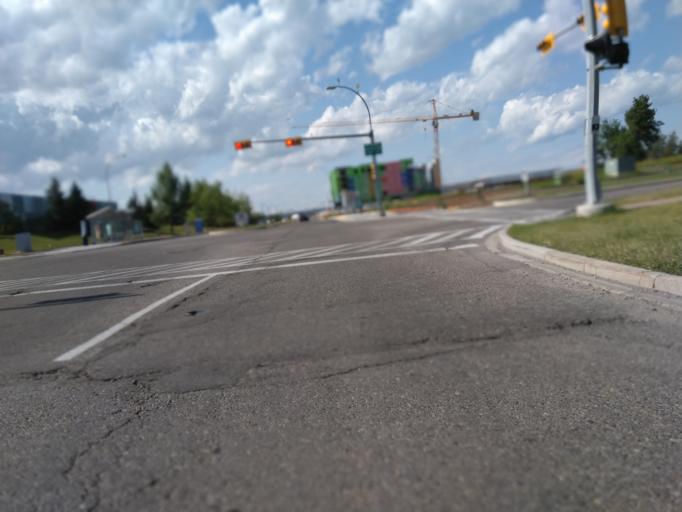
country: CA
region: Alberta
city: Calgary
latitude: 51.0750
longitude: -114.1452
